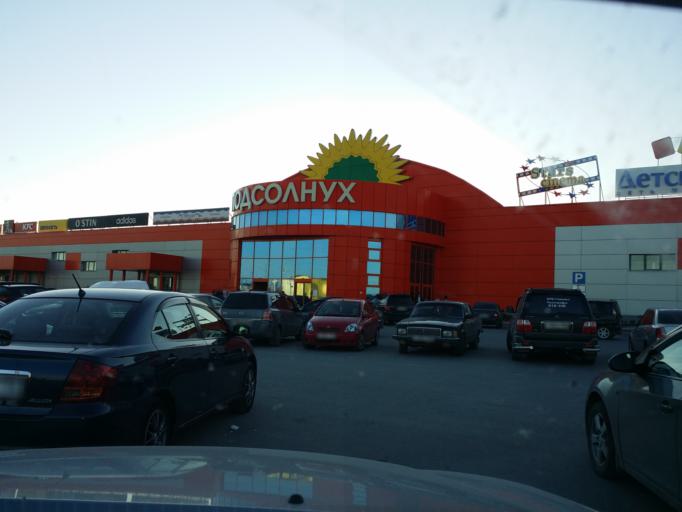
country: RU
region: Khanty-Mansiyskiy Avtonomnyy Okrug
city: Nizhnevartovsk
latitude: 60.9434
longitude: 76.6356
